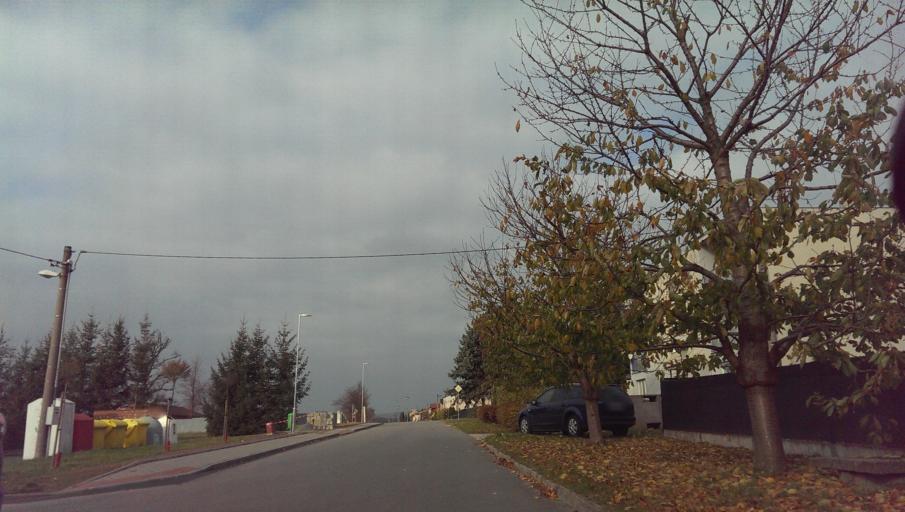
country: CZ
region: Zlin
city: Tlumacov
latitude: 49.2564
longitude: 17.5035
